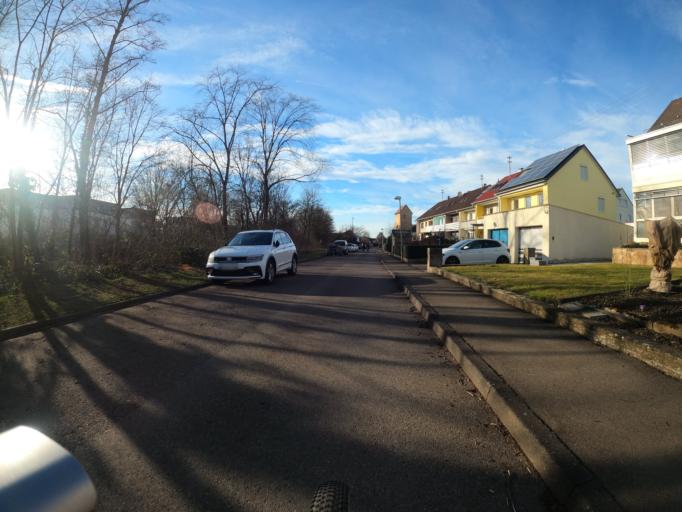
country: DE
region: Baden-Wuerttemberg
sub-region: Regierungsbezirk Stuttgart
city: Wendlingen am Neckar
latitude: 48.6703
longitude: 9.3964
